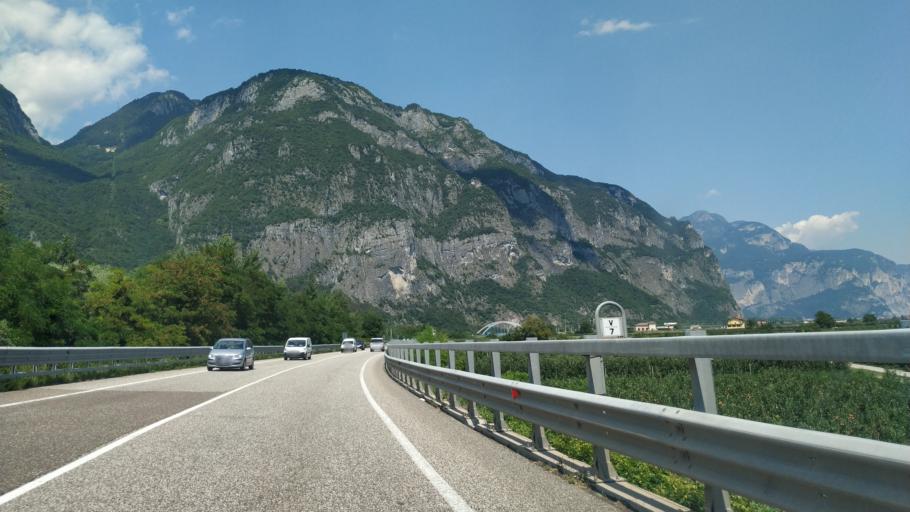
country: IT
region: Trentino-Alto Adige
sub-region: Provincia di Trento
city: Zambana
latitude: 46.1493
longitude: 11.0772
